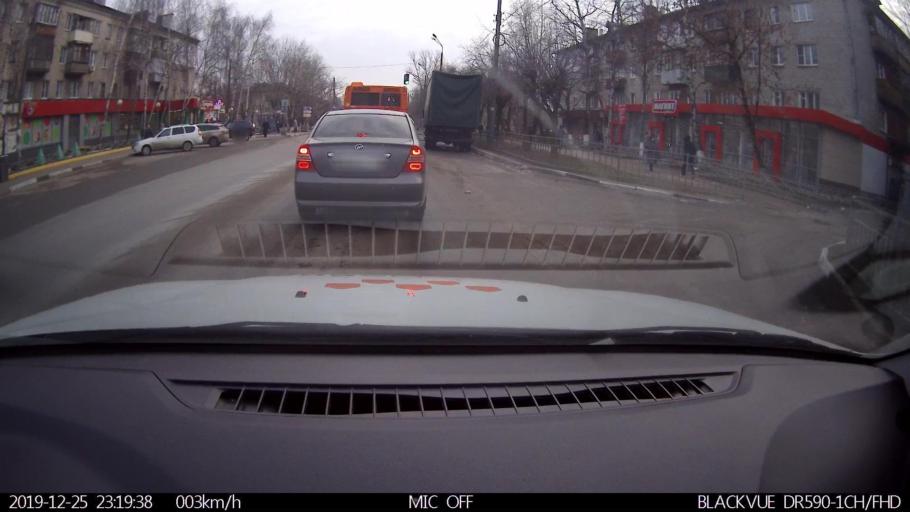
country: RU
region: Nizjnij Novgorod
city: Gorbatovka
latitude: 56.3543
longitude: 43.8317
